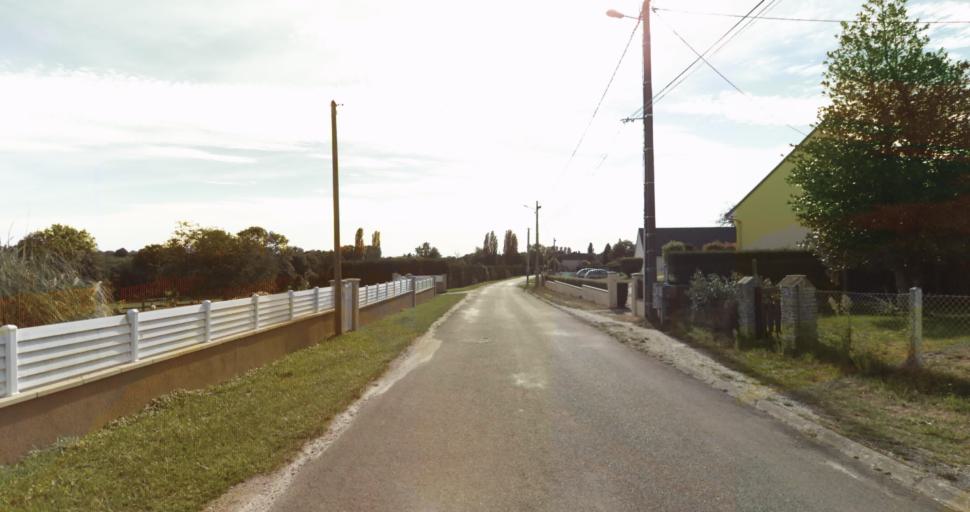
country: FR
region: Lower Normandy
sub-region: Departement de l'Orne
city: Gace
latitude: 48.7088
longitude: 0.2283
